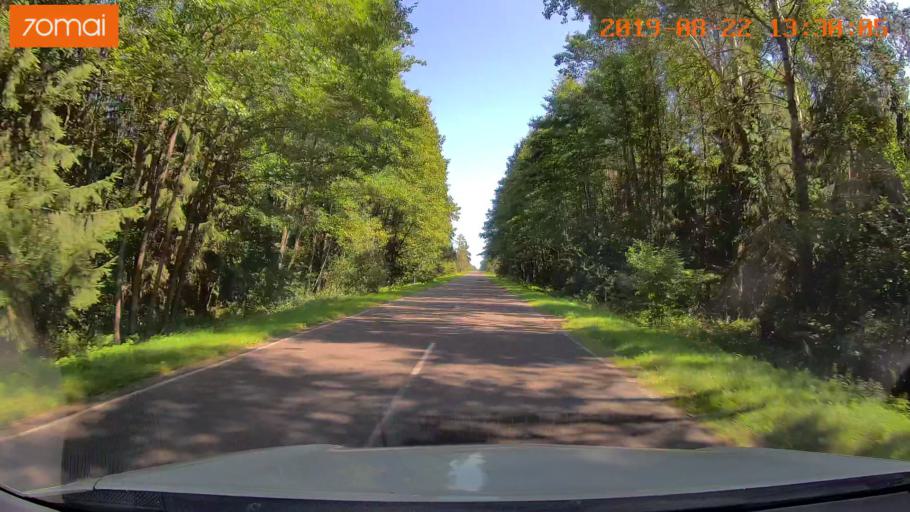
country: BY
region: Minsk
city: Staryya Darohi
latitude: 53.2173
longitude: 28.1475
